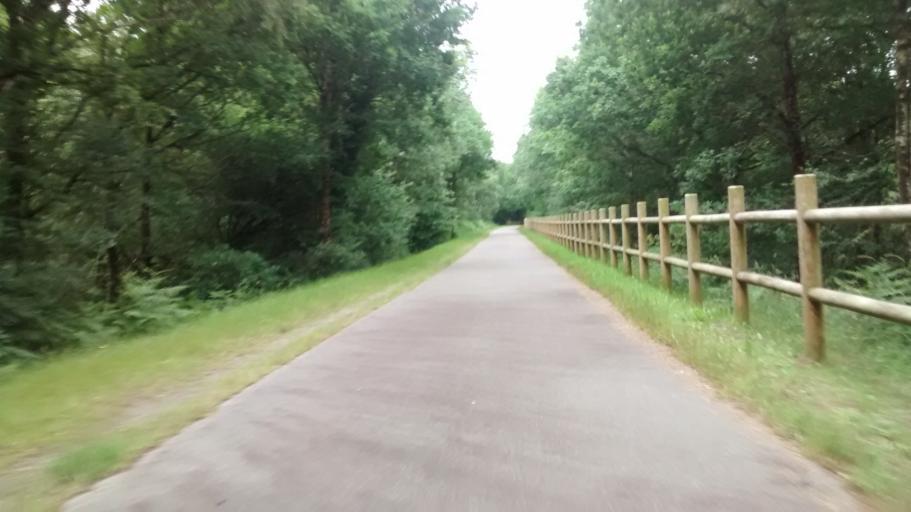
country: FR
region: Brittany
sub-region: Departement du Morbihan
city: Pleucadeuc
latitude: 47.7558
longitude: -2.4009
